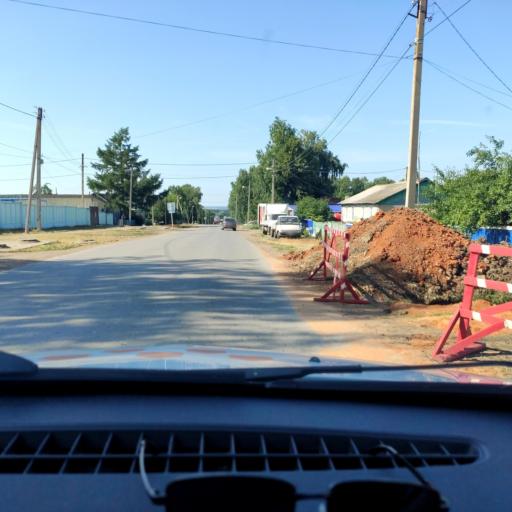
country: RU
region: Bashkortostan
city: Tolbazy
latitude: 54.0141
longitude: 55.8838
